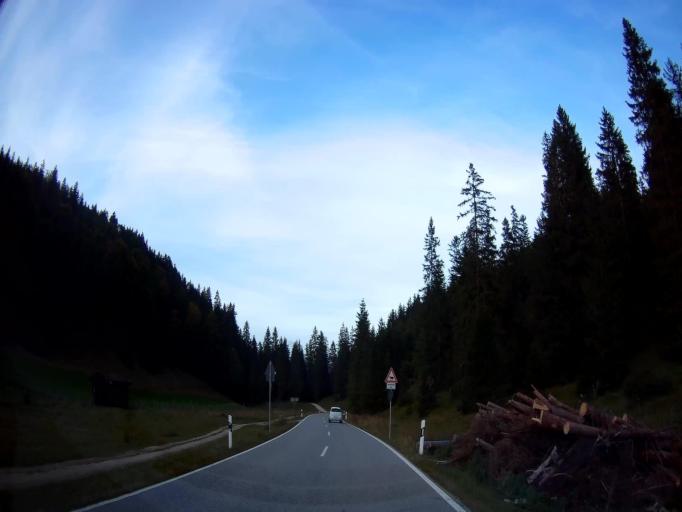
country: DE
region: Bavaria
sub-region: Upper Bavaria
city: Ramsau
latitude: 47.6281
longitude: 12.9061
